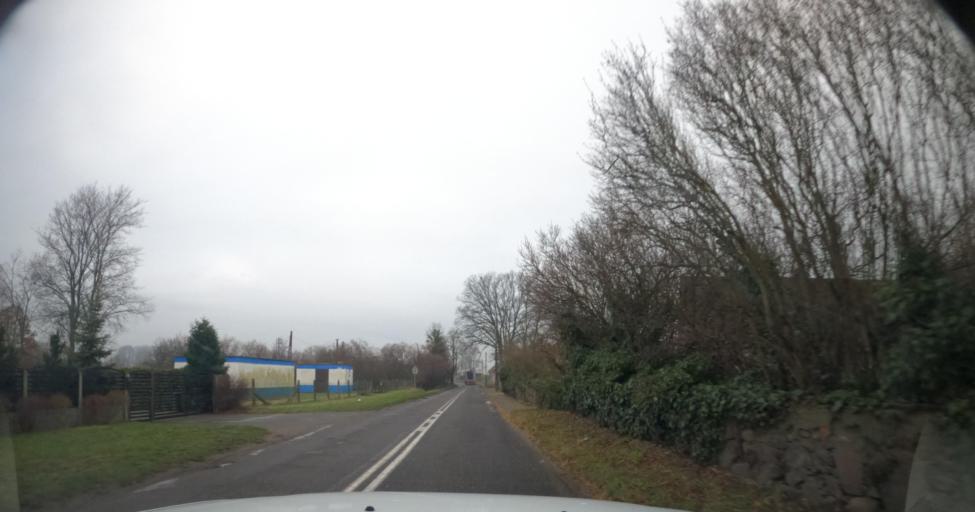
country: PL
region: West Pomeranian Voivodeship
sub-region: Powiat mysliborski
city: Boleszkowice
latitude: 52.7292
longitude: 14.5731
